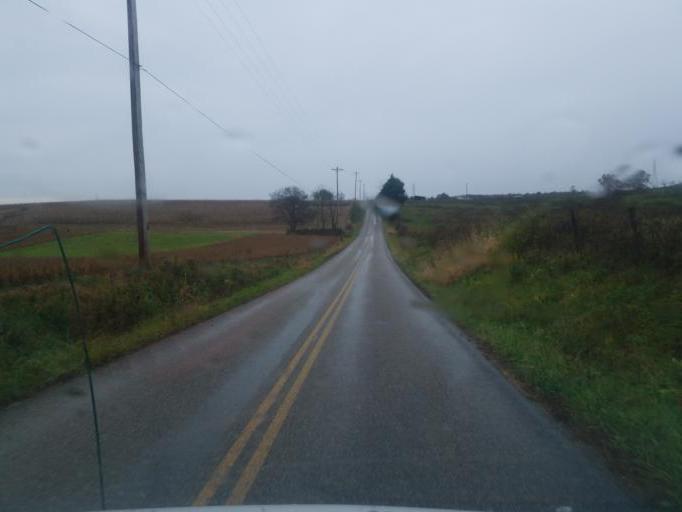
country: US
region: Ohio
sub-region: Washington County
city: Beverly
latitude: 39.4716
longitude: -81.7065
